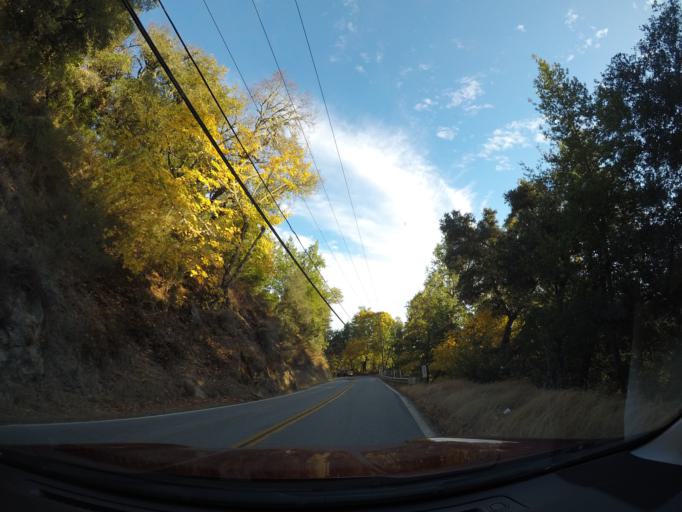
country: US
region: California
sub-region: Santa Clara County
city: Lexington Hills
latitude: 37.1663
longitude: -122.0205
